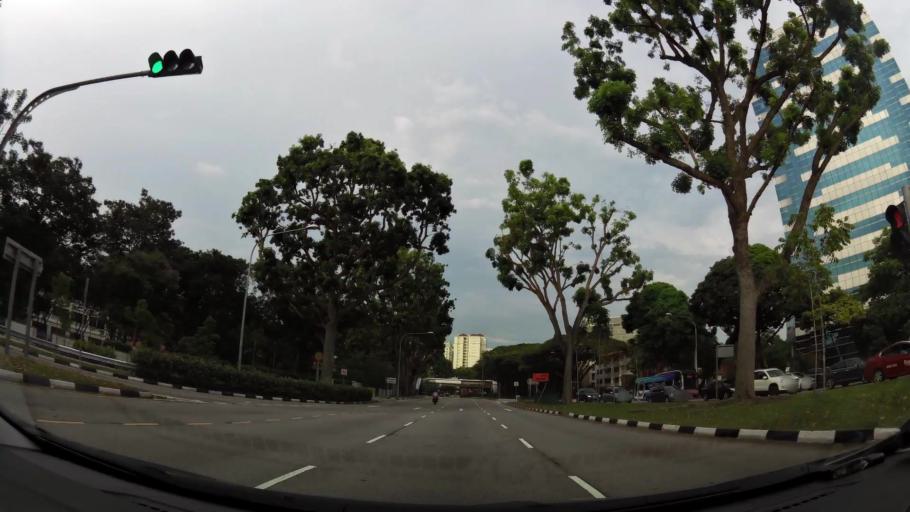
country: SG
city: Singapore
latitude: 1.2848
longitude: 103.8018
